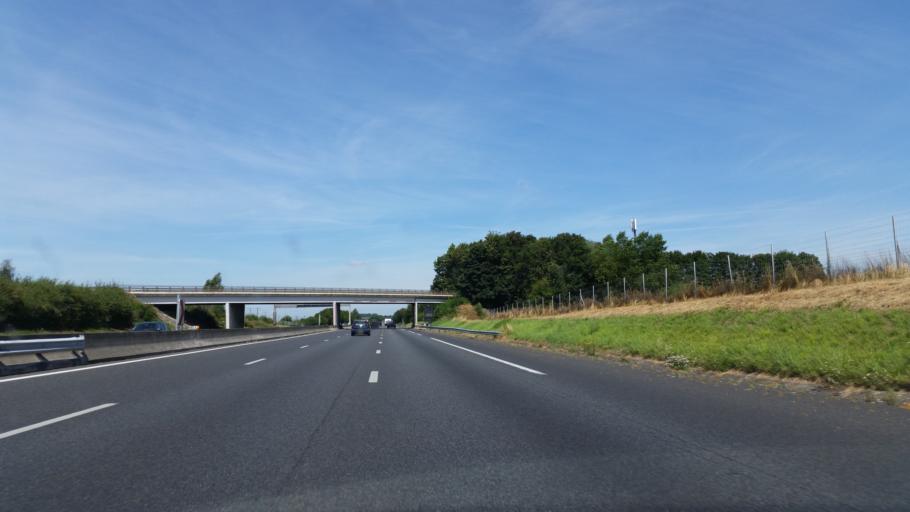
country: FR
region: Nord-Pas-de-Calais
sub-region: Departement du Pas-de-Calais
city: Bapaume
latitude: 50.1236
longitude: 2.8718
